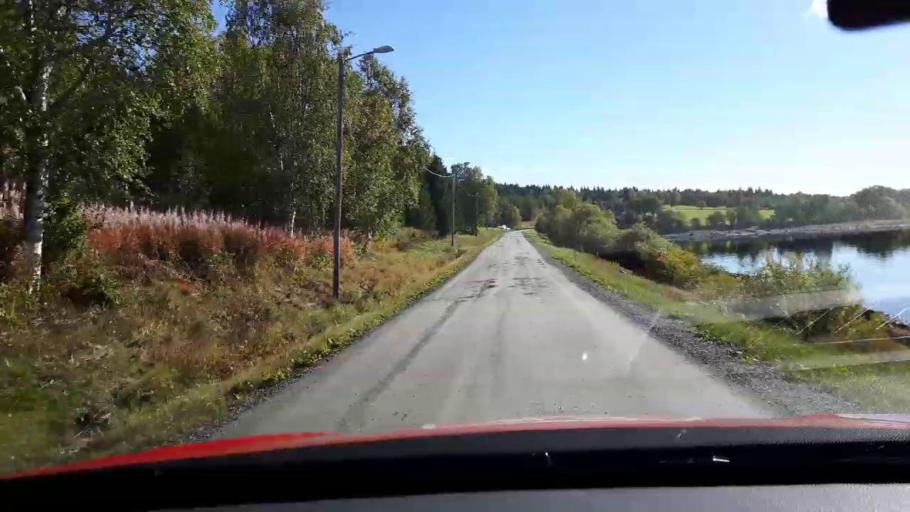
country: NO
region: Nord-Trondelag
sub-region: Lierne
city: Sandvika
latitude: 64.6455
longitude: 13.7678
